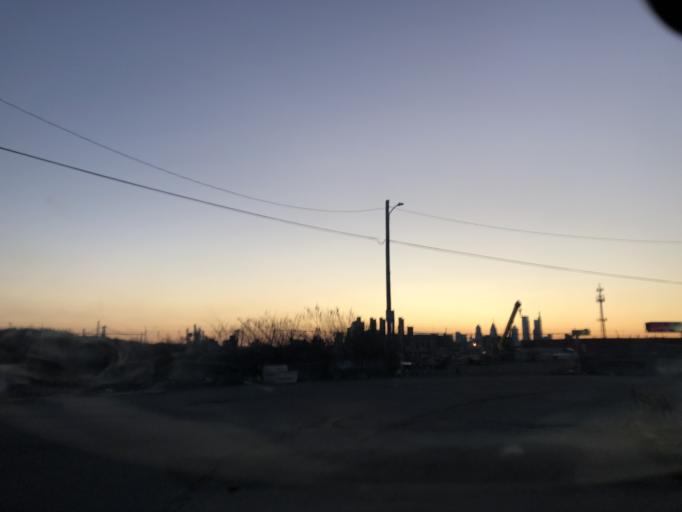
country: US
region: New Jersey
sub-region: Camden County
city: Camden
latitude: 39.9708
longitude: -75.1197
